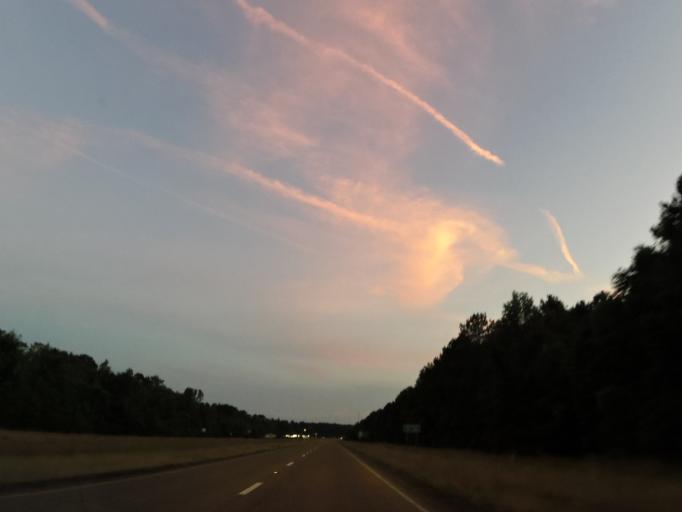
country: US
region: Mississippi
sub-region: Lauderdale County
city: Meridian Station
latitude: 32.5287
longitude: -88.5128
